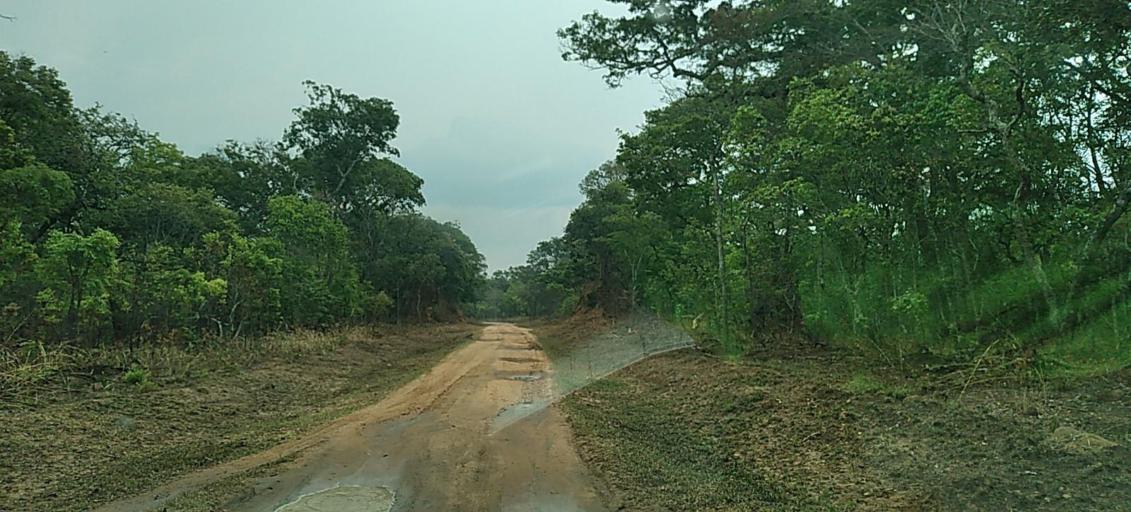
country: ZM
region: North-Western
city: Mwinilunga
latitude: -11.4665
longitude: 24.4726
